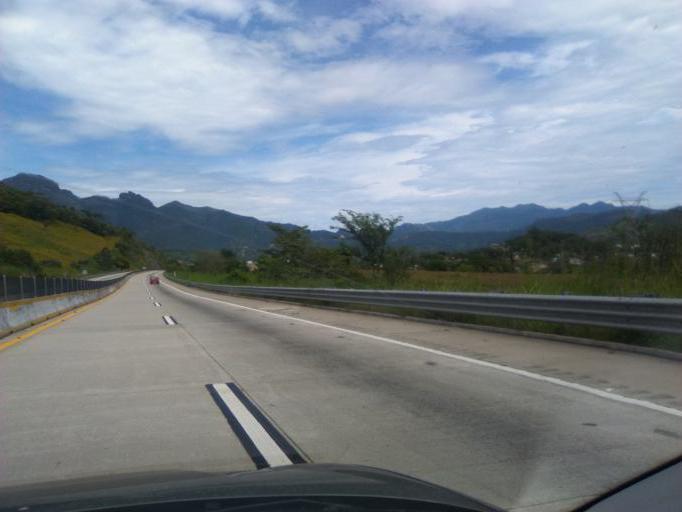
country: MX
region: Guerrero
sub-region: Chilpancingo de los Bravo
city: Mohoneras
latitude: 17.2399
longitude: -99.5237
